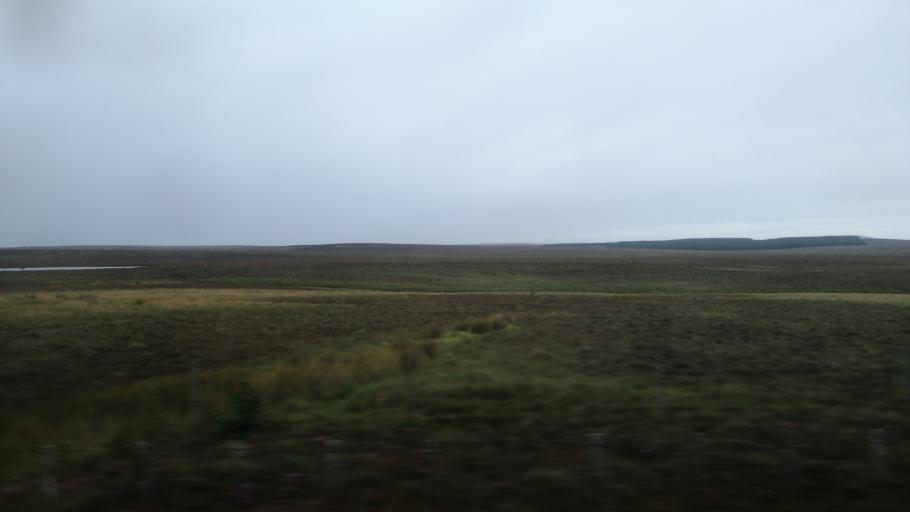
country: GB
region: Scotland
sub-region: Highland
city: Thurso
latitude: 58.3728
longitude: -3.7318
